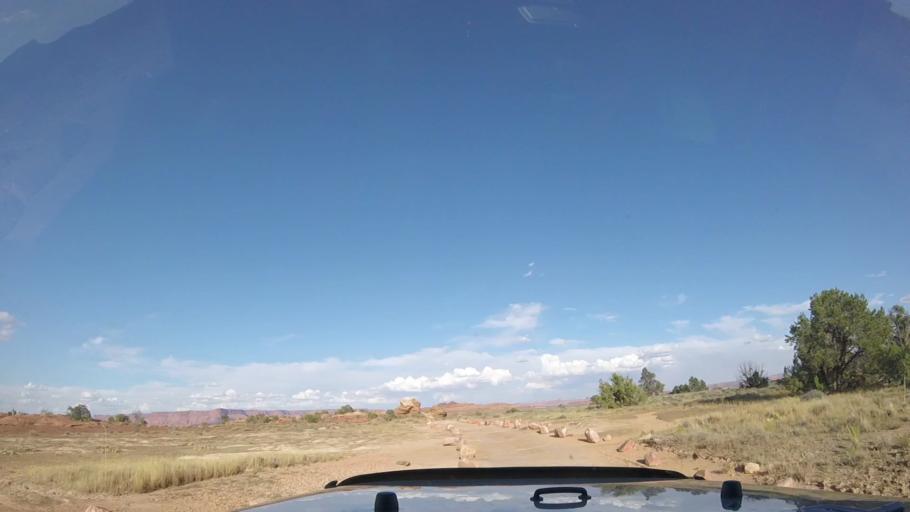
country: US
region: Utah
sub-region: Grand County
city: Moab
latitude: 38.2125
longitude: -109.8095
